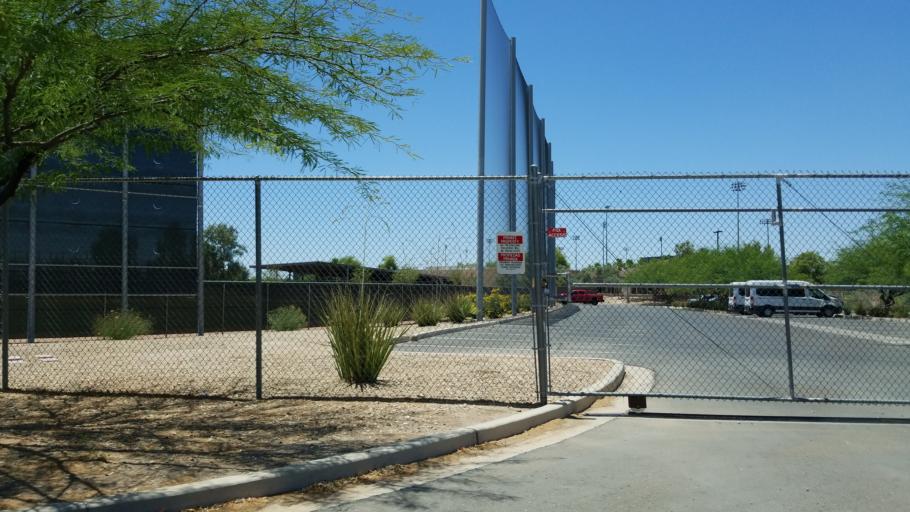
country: US
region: Arizona
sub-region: Maricopa County
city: Tolleson
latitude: 33.5123
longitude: -112.2908
